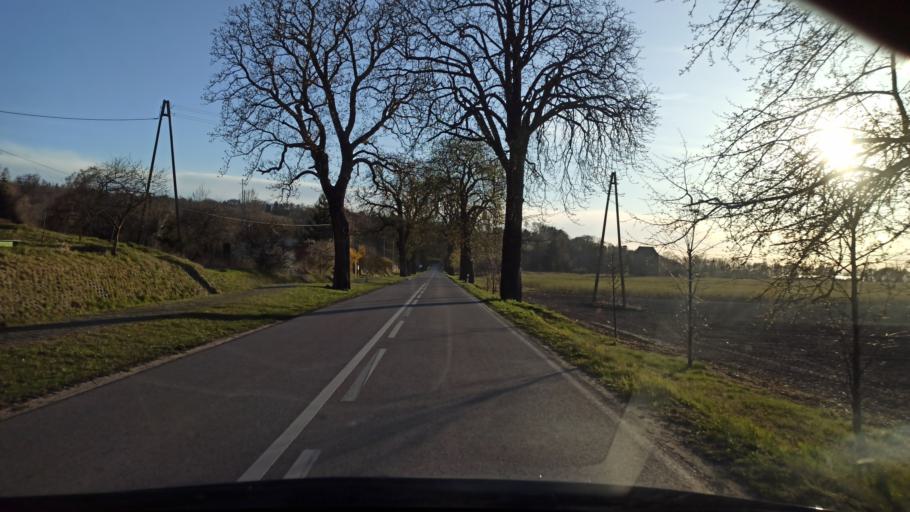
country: PL
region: Warmian-Masurian Voivodeship
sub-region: Powiat elblaski
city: Tolkmicko
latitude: 54.2943
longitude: 19.4841
